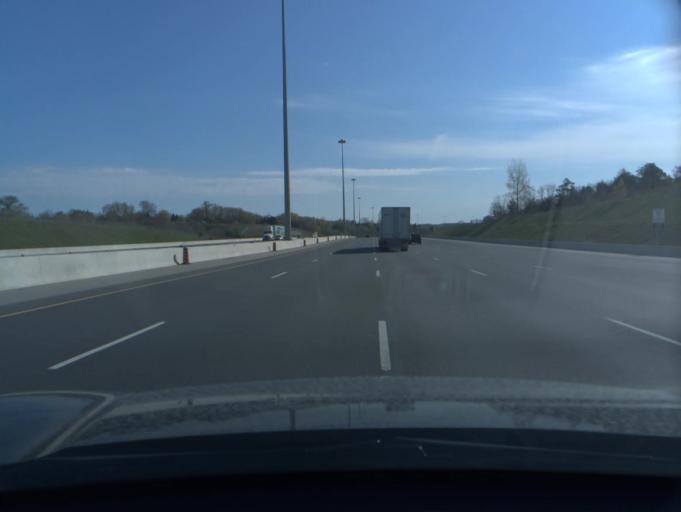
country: CA
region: Ontario
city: North Perth
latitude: 43.8163
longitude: -80.9998
